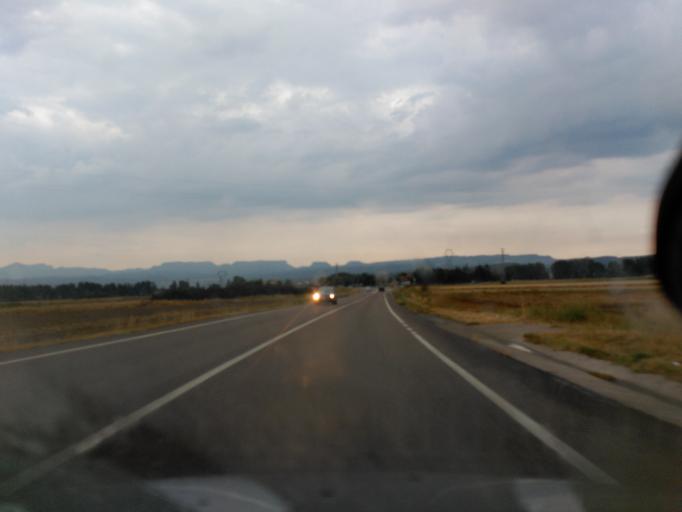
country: ES
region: Catalonia
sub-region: Provincia de Barcelona
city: Manlleu
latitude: 41.9598
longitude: 2.2879
